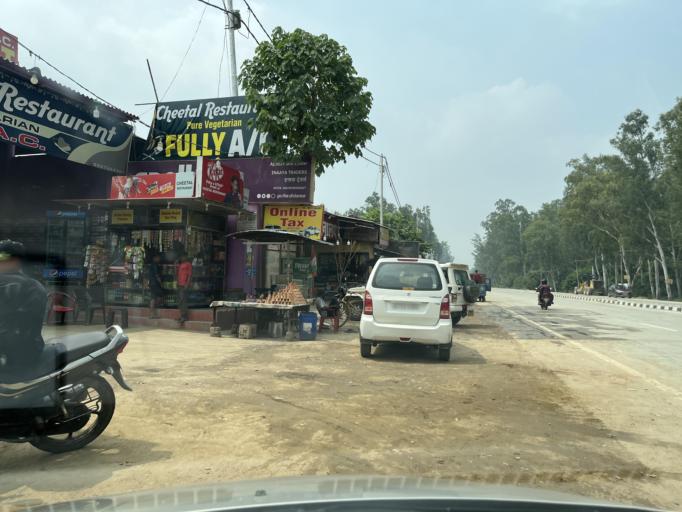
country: IN
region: Uttarakhand
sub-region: Haridwar
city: Sultanpur
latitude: 29.7474
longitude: 78.2598
